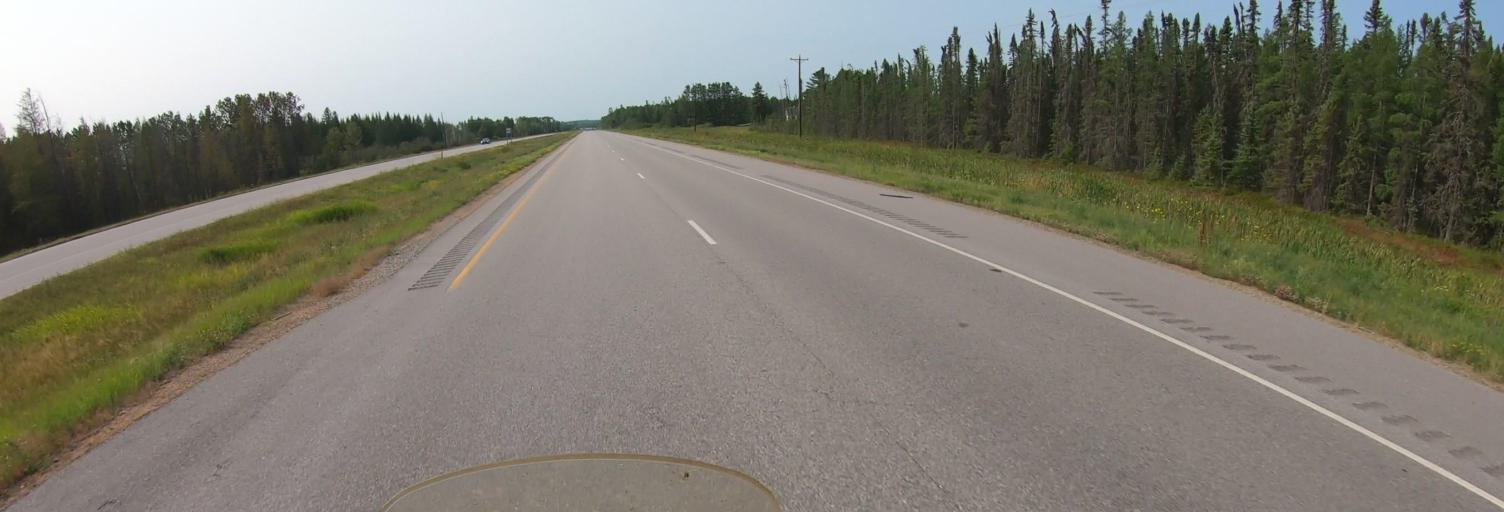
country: US
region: Minnesota
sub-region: Saint Louis County
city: Mountain Iron
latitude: 47.8319
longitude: -92.6747
